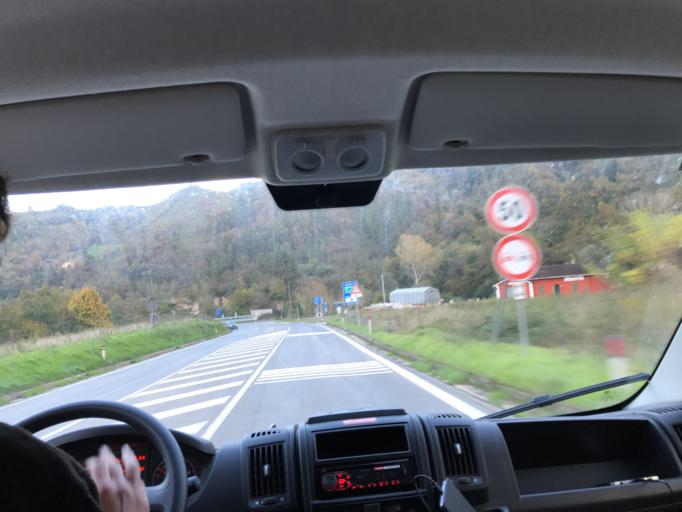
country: IT
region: The Marches
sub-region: Provincia di Ascoli Piceno
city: Marsia
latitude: 42.8217
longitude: 13.5066
